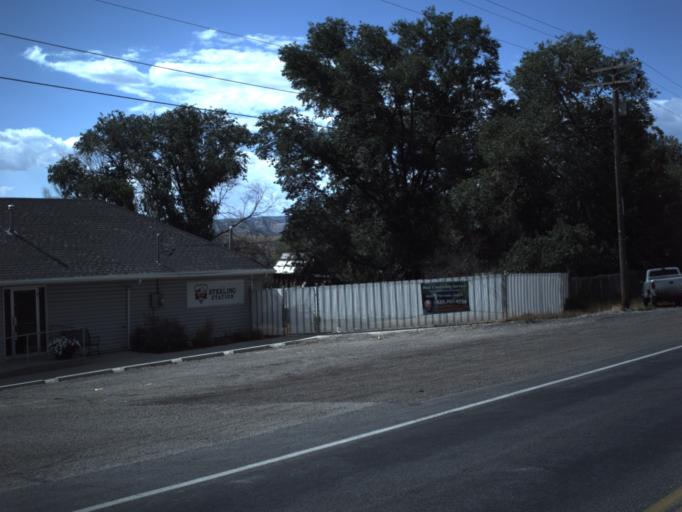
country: US
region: Utah
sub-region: Sanpete County
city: Manti
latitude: 39.1951
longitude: -111.6925
